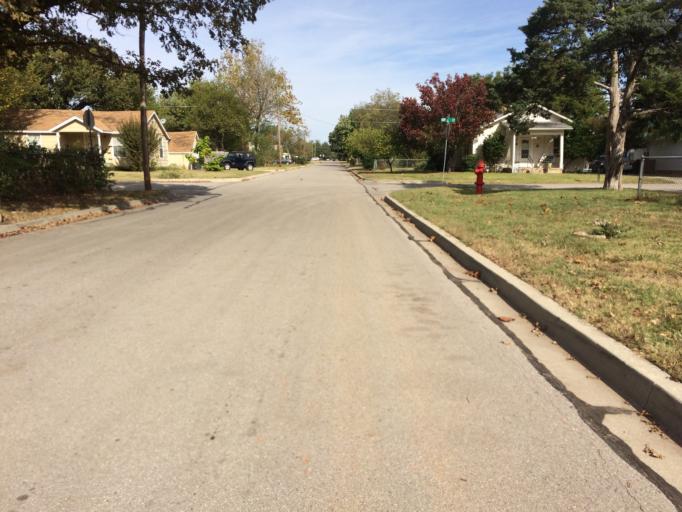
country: US
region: Oklahoma
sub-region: Cleveland County
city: Norman
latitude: 35.2303
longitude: -97.4479
